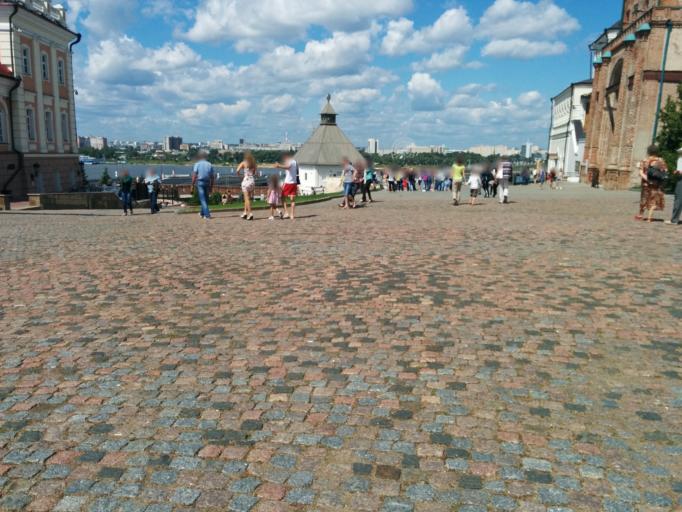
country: RU
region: Tatarstan
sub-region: Gorod Kazan'
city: Kazan
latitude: 55.8000
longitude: 49.1051
